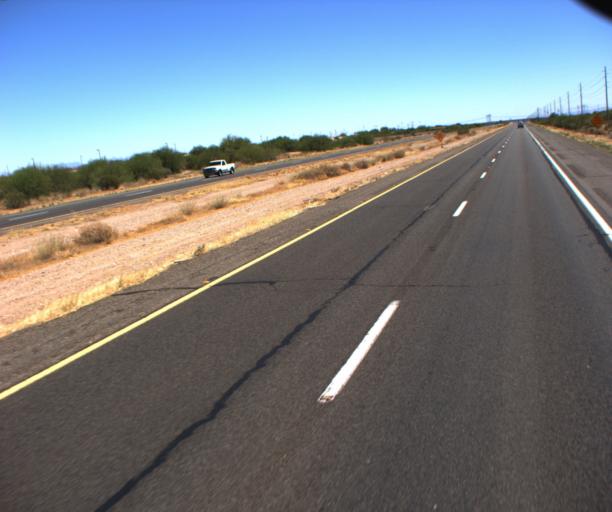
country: US
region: Arizona
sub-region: Maricopa County
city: Sun City West
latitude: 33.7018
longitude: -112.4314
